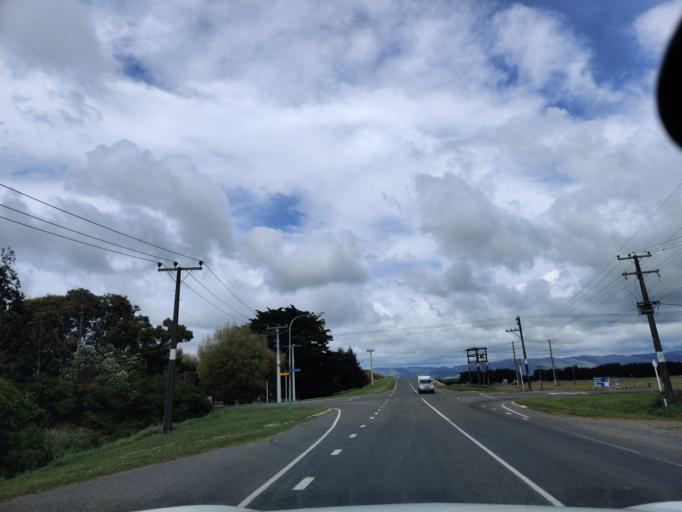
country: NZ
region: Manawatu-Wanganui
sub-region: Palmerston North City
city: Palmerston North
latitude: -40.3651
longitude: 175.5514
